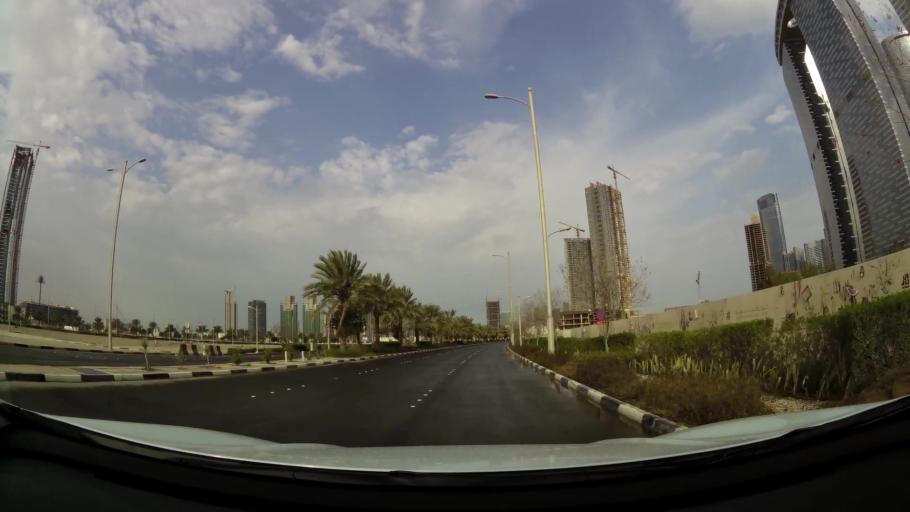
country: AE
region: Abu Dhabi
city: Abu Dhabi
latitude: 24.4908
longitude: 54.4091
